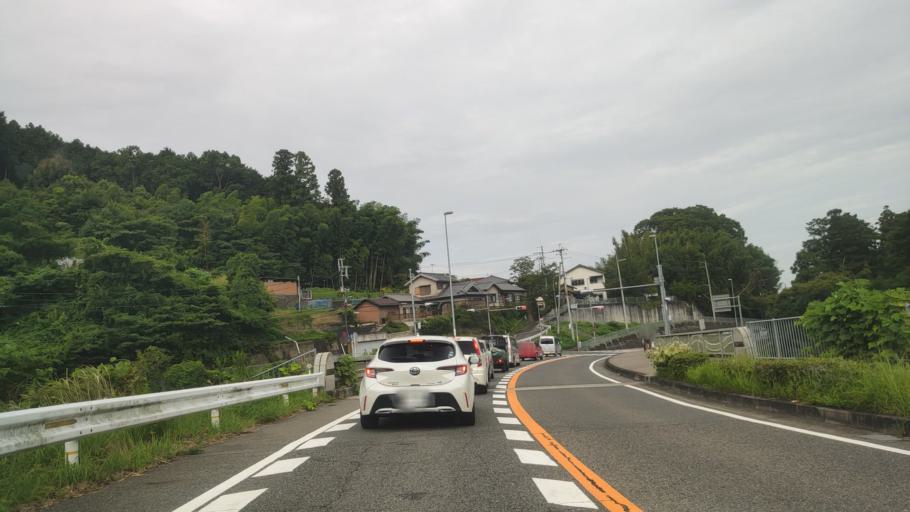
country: JP
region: Osaka
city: Tondabayashicho
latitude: 34.4217
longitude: 135.5789
